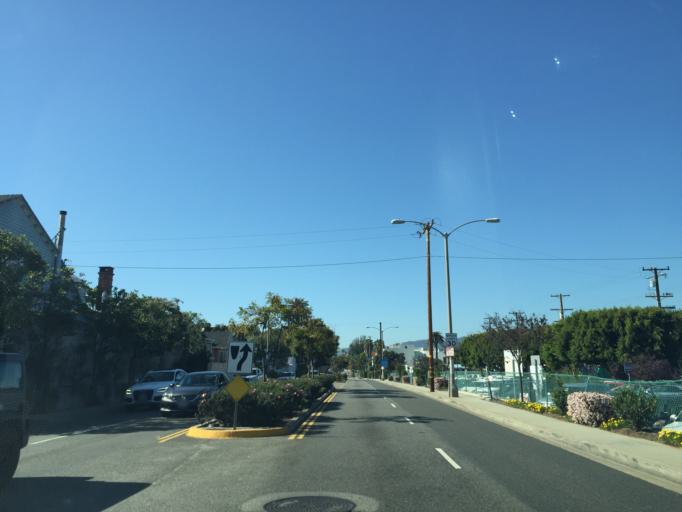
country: US
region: California
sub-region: Los Angeles County
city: Santa Monica
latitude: 34.0029
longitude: -118.4855
